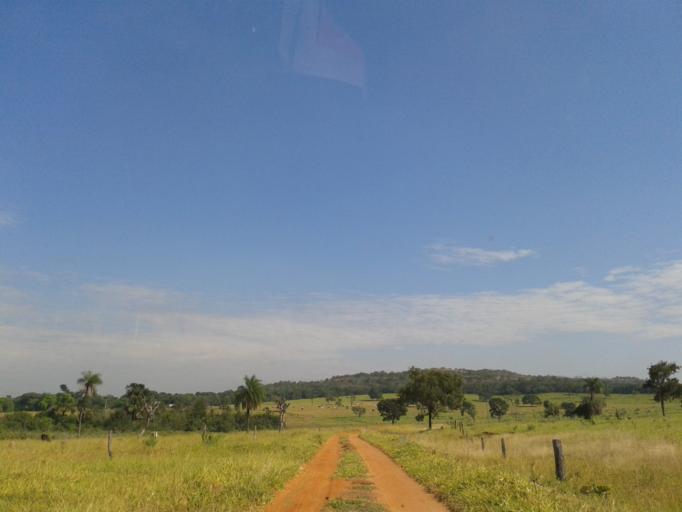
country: BR
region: Minas Gerais
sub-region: Campina Verde
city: Campina Verde
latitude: -19.3911
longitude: -49.6293
